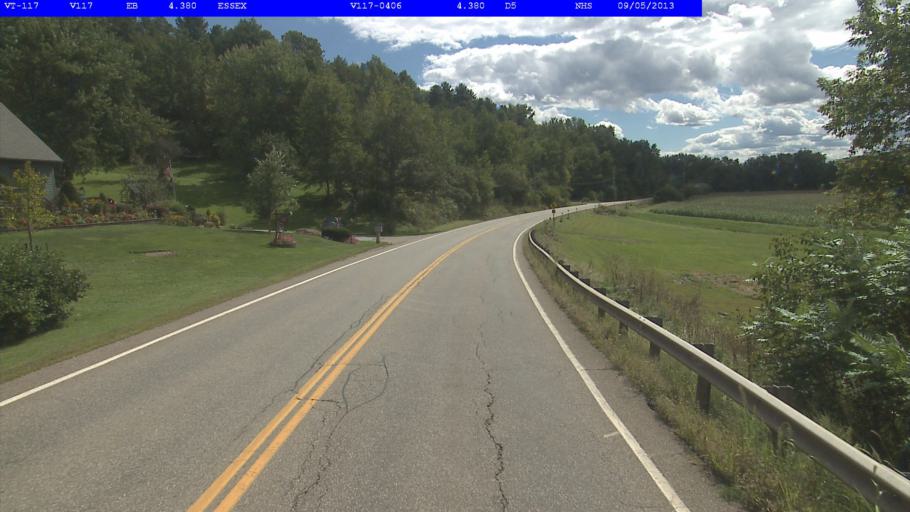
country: US
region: Vermont
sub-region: Chittenden County
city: Jericho
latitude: 44.4715
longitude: -73.0307
